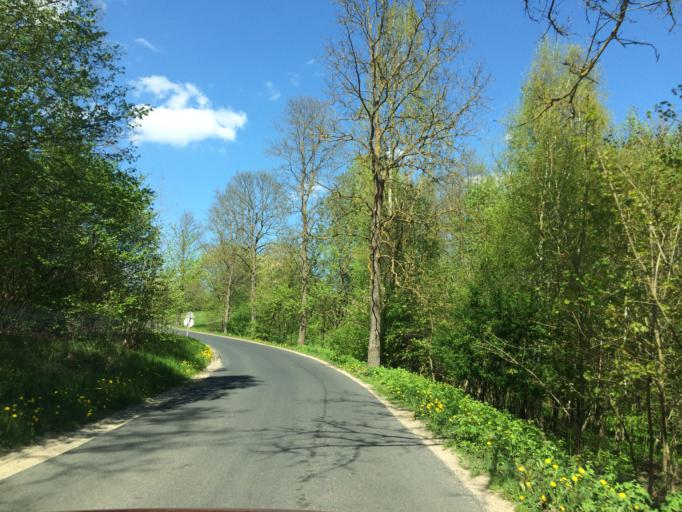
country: PL
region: Warmian-Masurian Voivodeship
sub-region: Powiat ilawski
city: Lubawa
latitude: 53.4012
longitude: 19.7460
